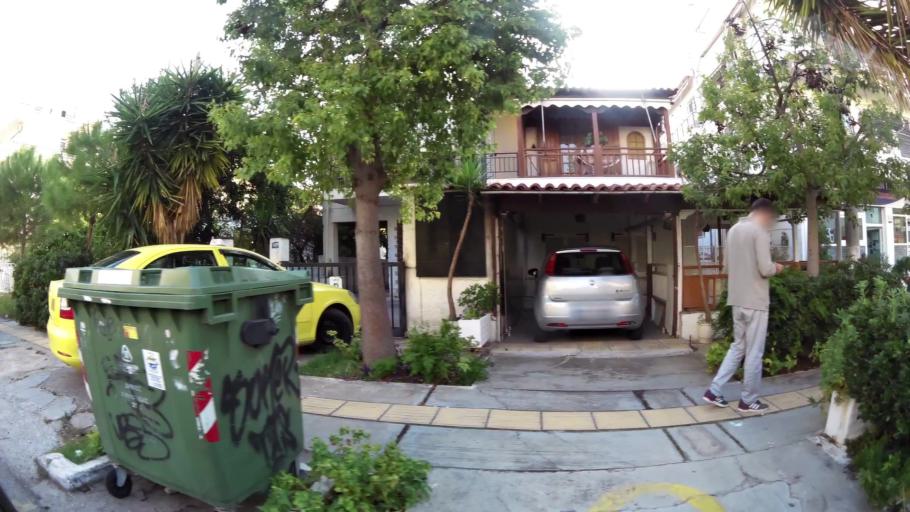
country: GR
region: Attica
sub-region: Nomarchia Athinas
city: Argyroupoli
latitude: 37.8989
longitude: 23.7706
